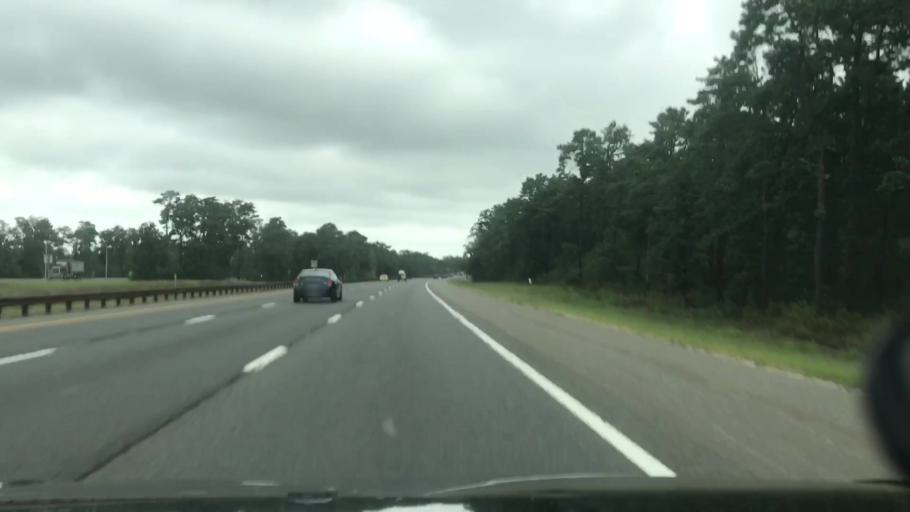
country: US
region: New Jersey
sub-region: Ocean County
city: South Toms River
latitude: 39.9071
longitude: -74.2119
